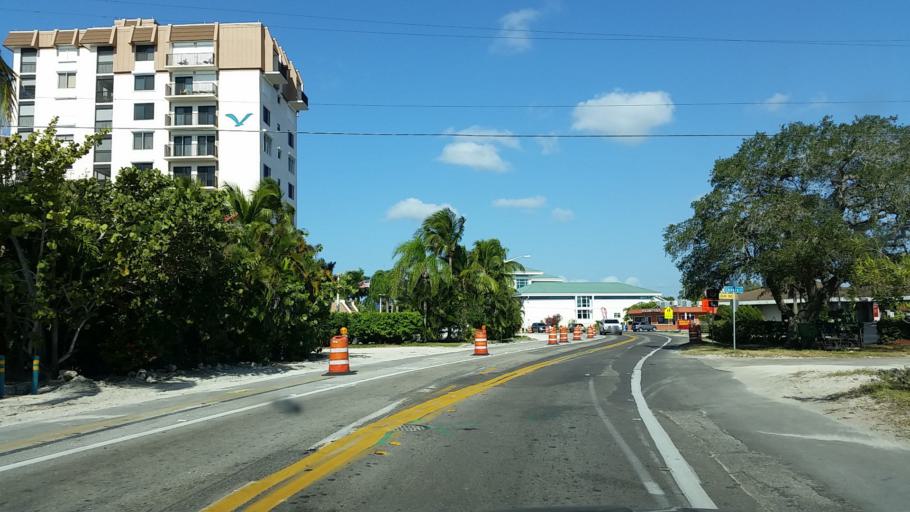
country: US
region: Florida
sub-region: Lee County
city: Fort Myers Beach
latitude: 26.4463
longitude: -81.9378
